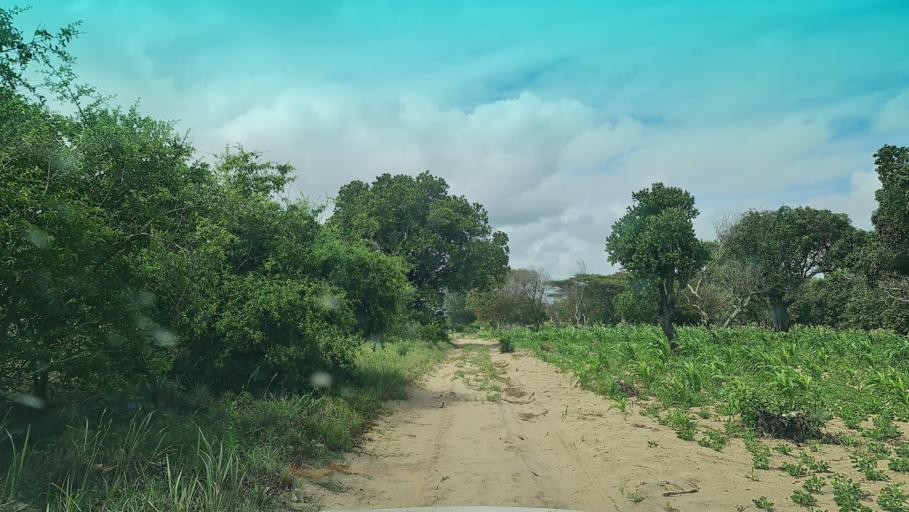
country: EG
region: Aswan
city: Idfu
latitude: 25.3980
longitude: 33.0275
